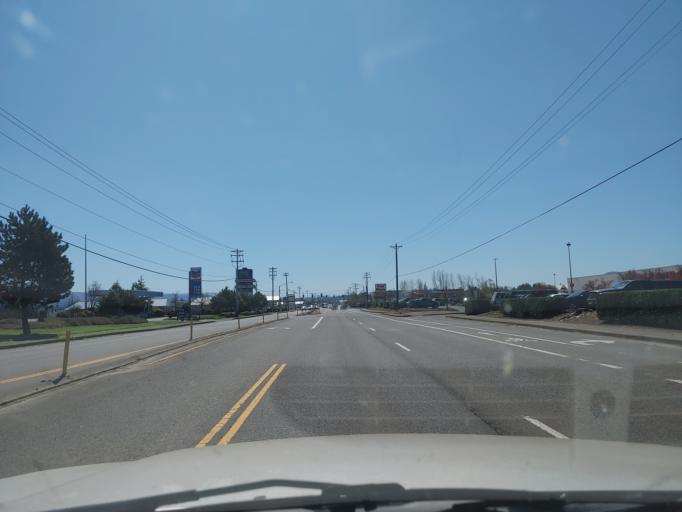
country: US
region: Oregon
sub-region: Tillamook County
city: Tillamook
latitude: 45.4754
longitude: -123.8444
